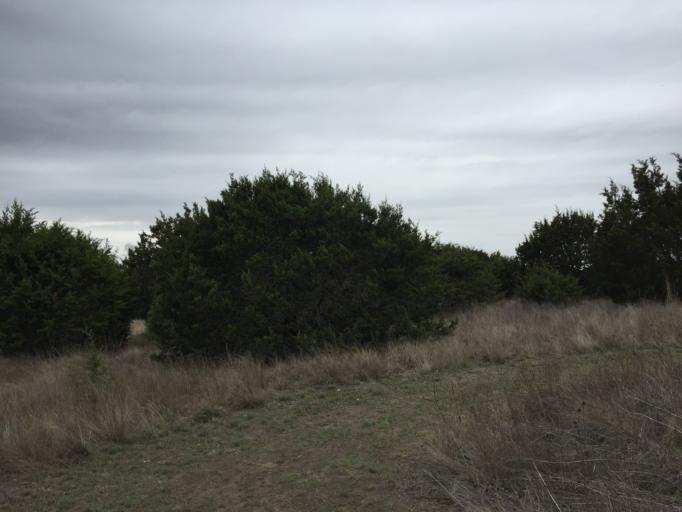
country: US
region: Texas
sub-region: Bell County
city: Fort Hood
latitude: 31.1183
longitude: -97.8146
